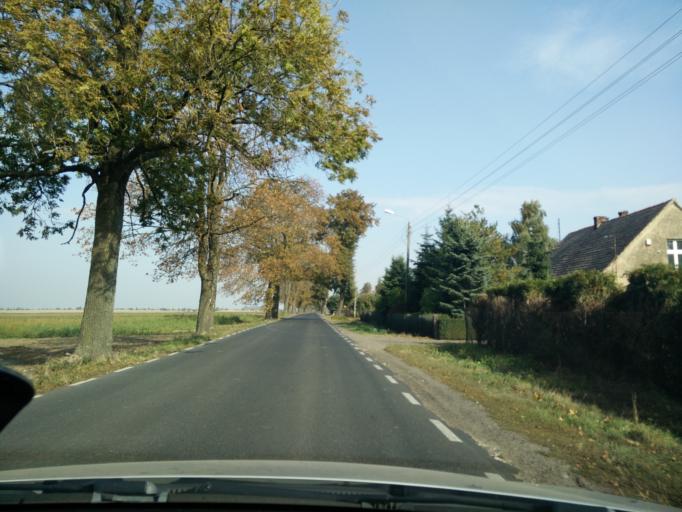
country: PL
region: Greater Poland Voivodeship
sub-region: Powiat sredzki
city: Sroda Wielkopolska
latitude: 52.2458
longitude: 17.2930
